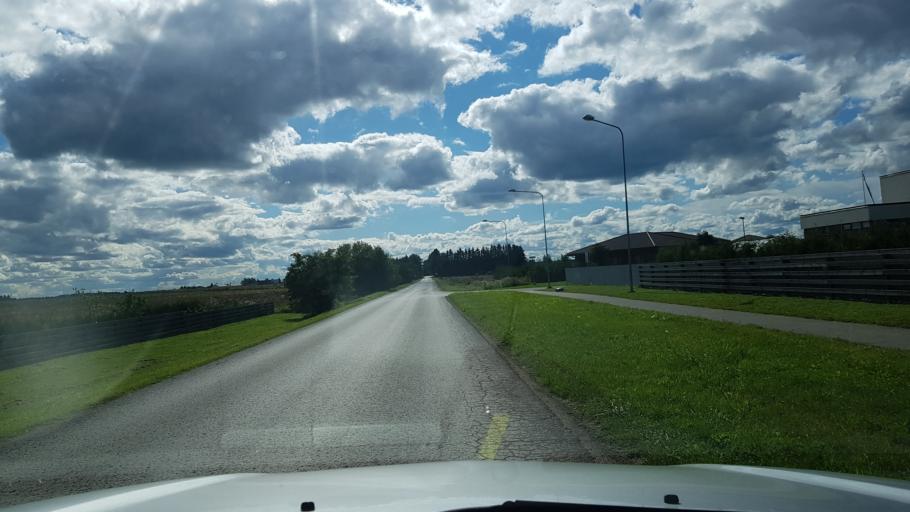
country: EE
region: Harju
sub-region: Kiili vald
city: Kiili
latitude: 59.3805
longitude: 24.8204
